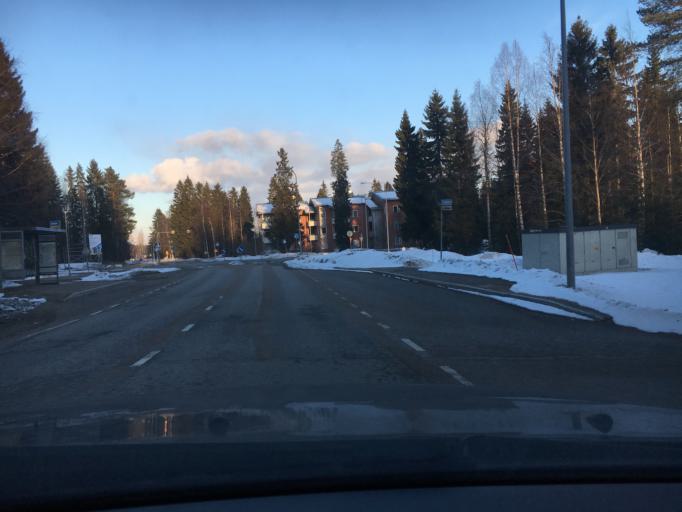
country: FI
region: Kainuu
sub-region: Kajaani
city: Kajaani
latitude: 64.2301
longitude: 27.7514
